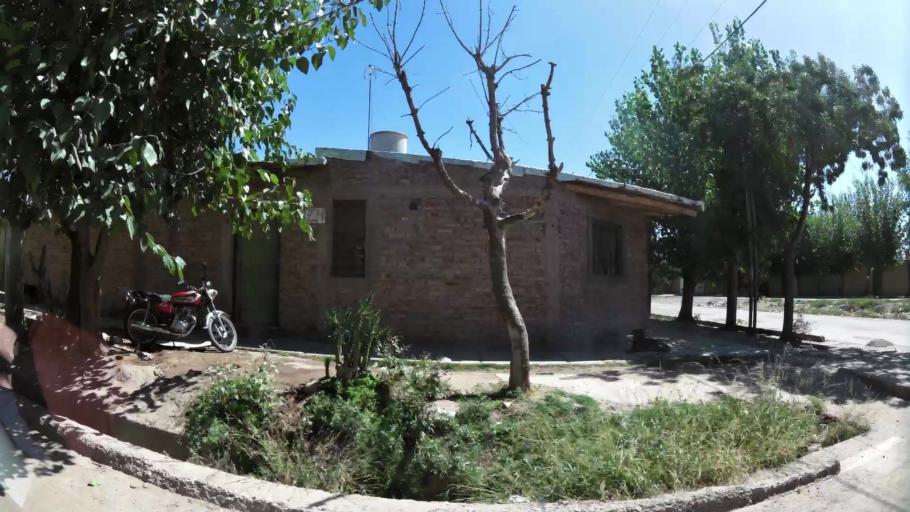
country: AR
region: Mendoza
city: Villa Nueva
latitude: -32.8760
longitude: -68.7970
